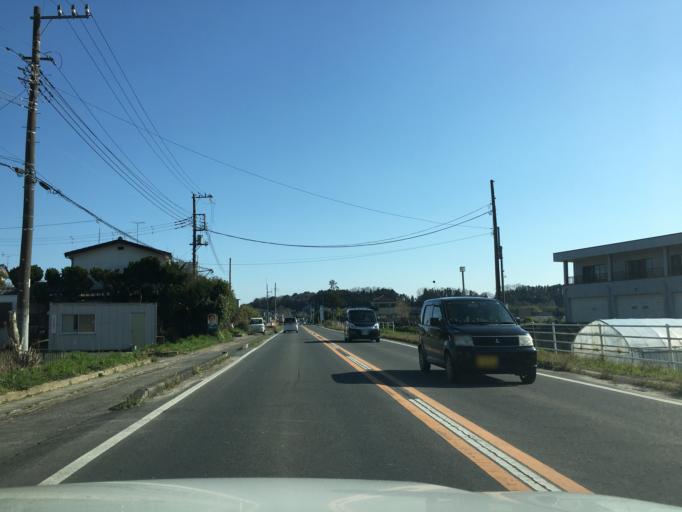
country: JP
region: Ibaraki
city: Omiya
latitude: 36.4485
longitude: 140.4096
